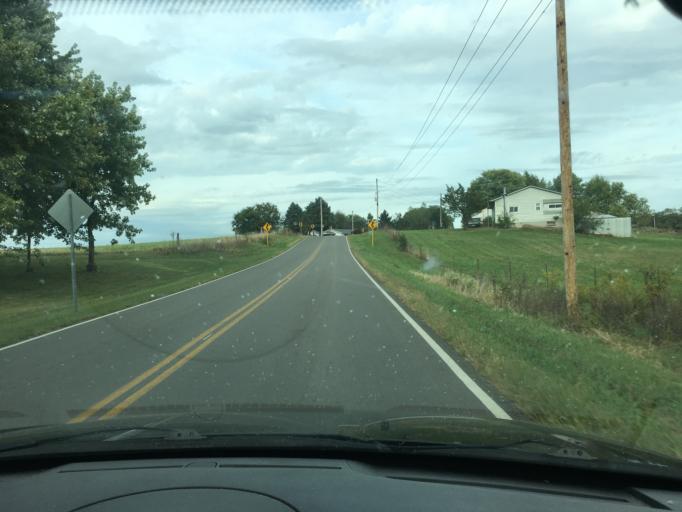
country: US
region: Ohio
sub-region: Logan County
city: Bellefontaine
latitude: 40.3122
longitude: -83.8003
